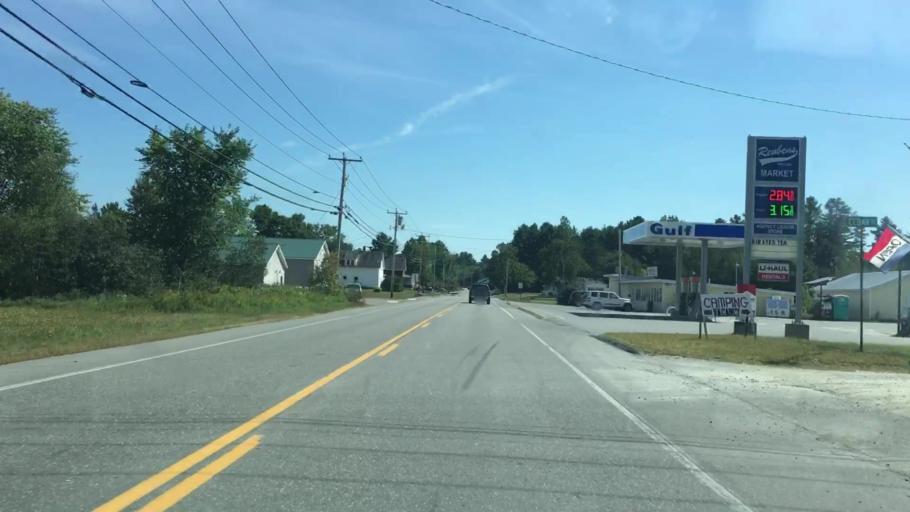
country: US
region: Maine
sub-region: Piscataquis County
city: Milo
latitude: 45.2458
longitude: -68.9766
